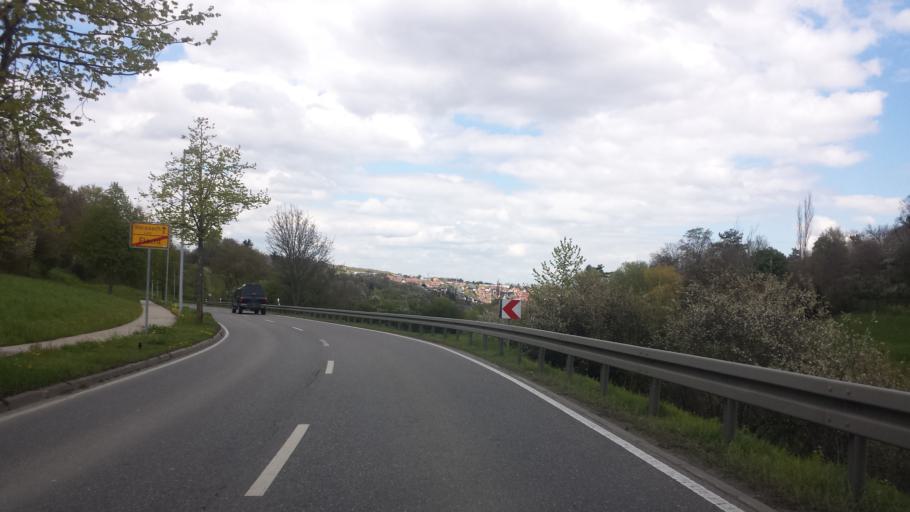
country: DE
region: Baden-Wuerttemberg
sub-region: Regierungsbezirk Stuttgart
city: Weissach
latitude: 48.8383
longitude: 8.9158
